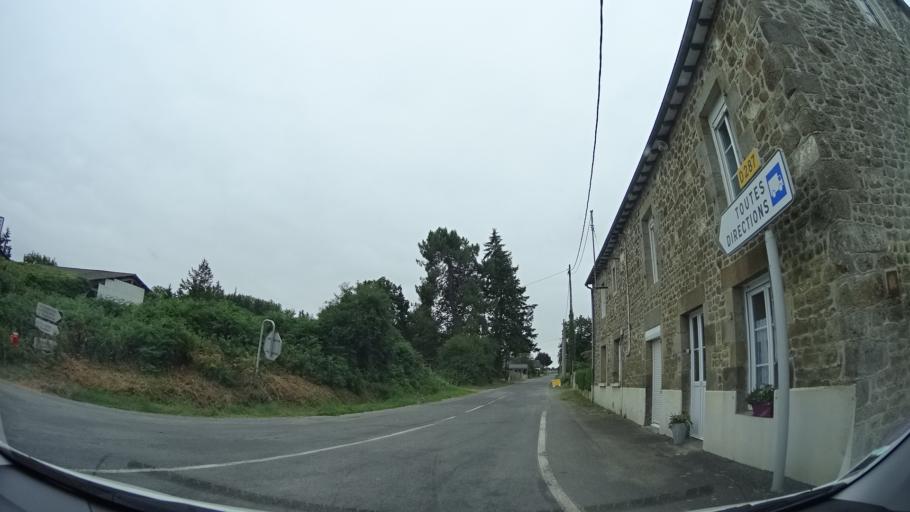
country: FR
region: Brittany
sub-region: Departement d'Ille-et-Vilaine
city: Hede-Bazouges
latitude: 48.2987
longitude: -1.7675
